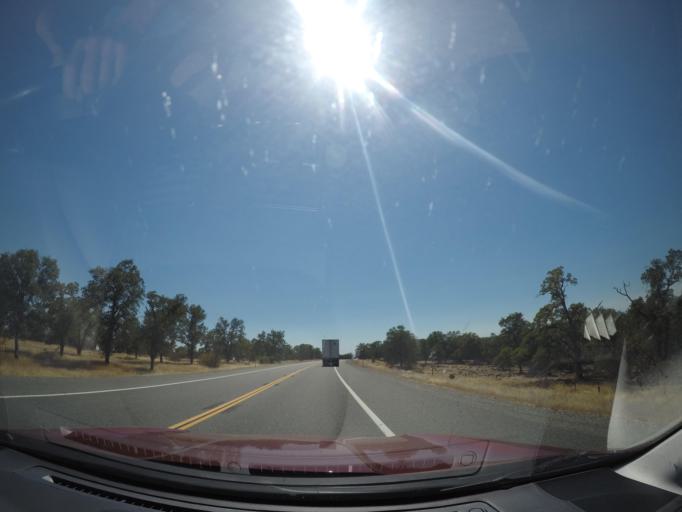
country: US
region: California
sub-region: Shasta County
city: Bella Vista
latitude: 40.6927
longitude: -122.1100
